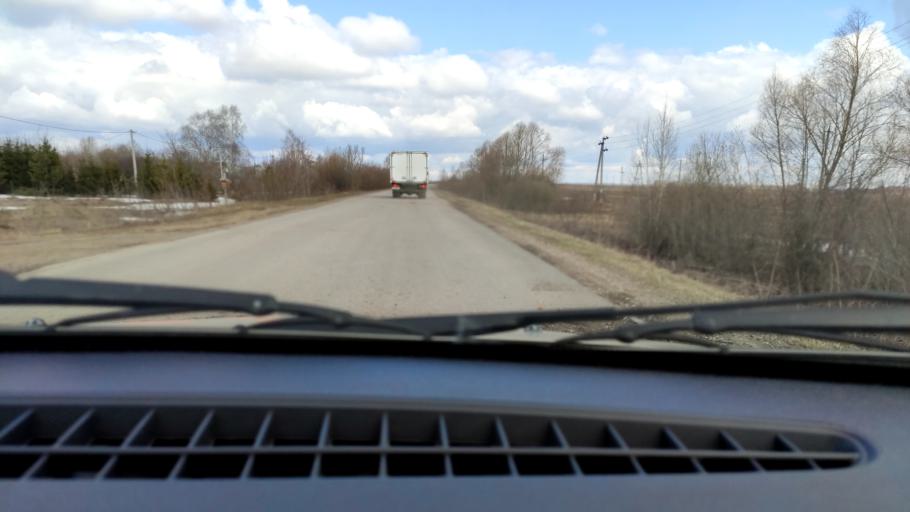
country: RU
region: Bashkortostan
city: Kudeyevskiy
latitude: 54.8304
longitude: 56.7931
